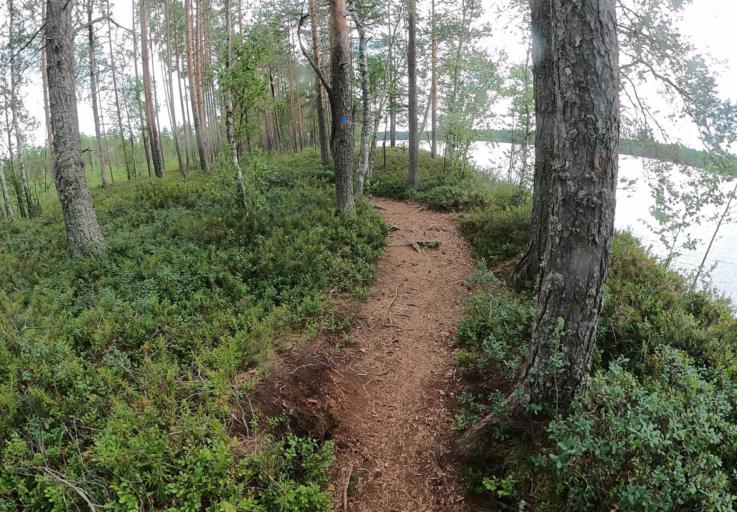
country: FI
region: North Karelia
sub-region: Joensuu
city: Joensuu
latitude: 62.6387
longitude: 29.8300
